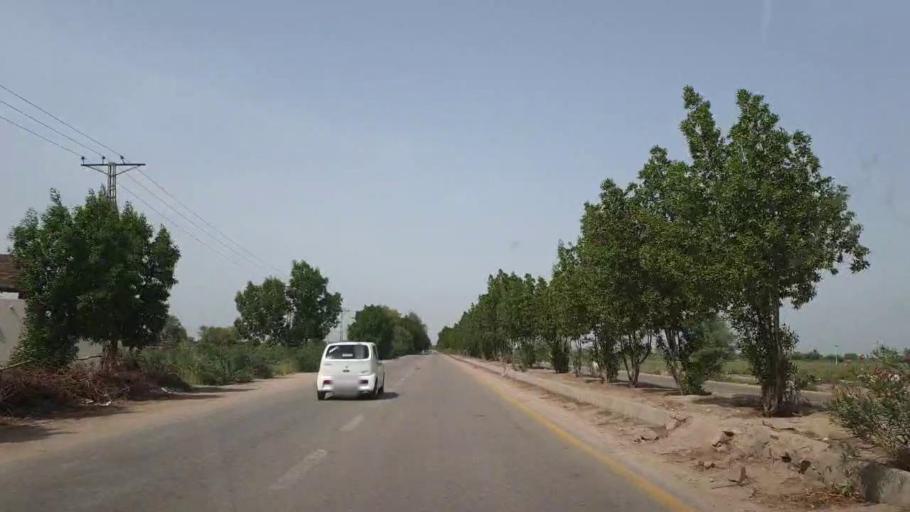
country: PK
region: Sindh
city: Sakrand
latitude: 26.1639
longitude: 68.2788
